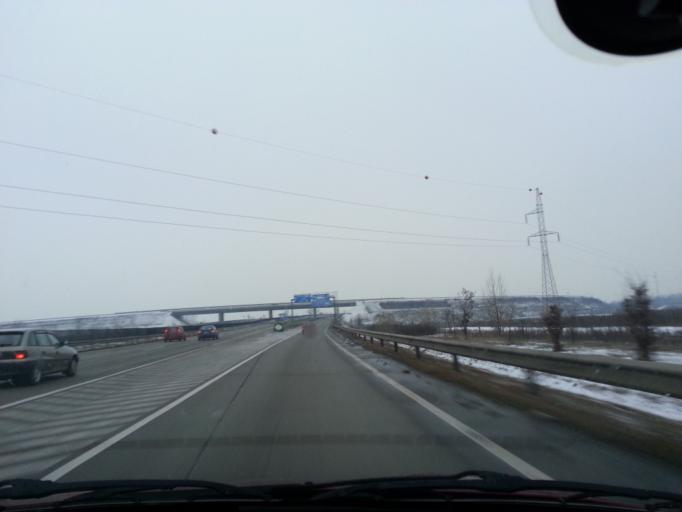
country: HU
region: Pest
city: Felsopakony
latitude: 47.3559
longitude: 19.2081
